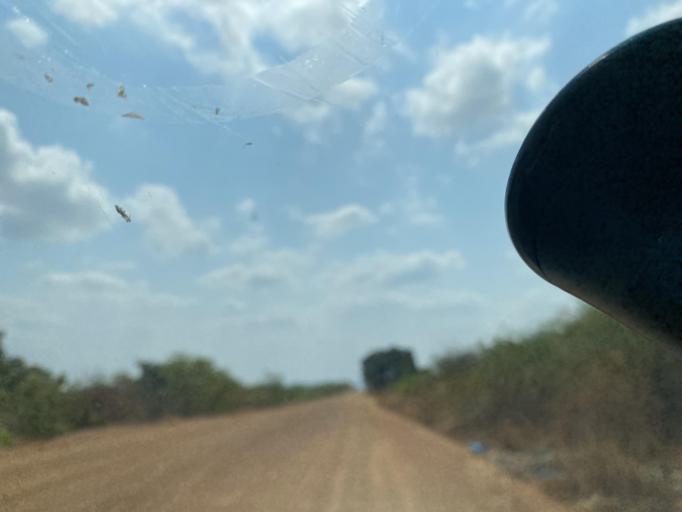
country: ZM
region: Lusaka
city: Chongwe
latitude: -15.5927
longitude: 28.7922
